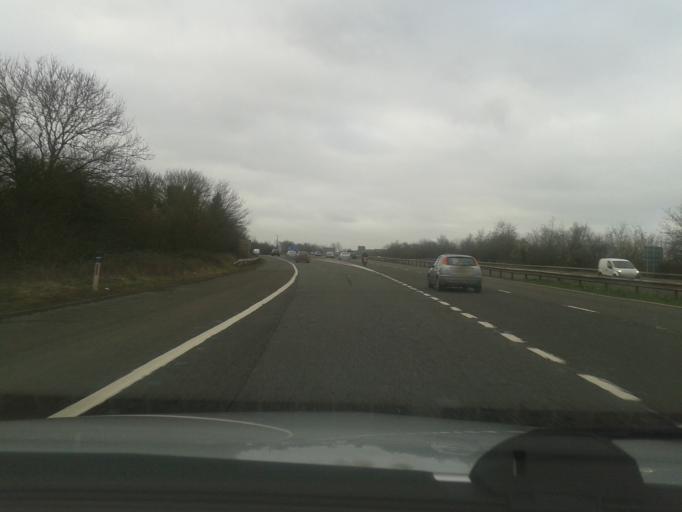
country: GB
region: England
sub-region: South Gloucestershire
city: Stoke Gifford
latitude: 51.5092
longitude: -2.5244
